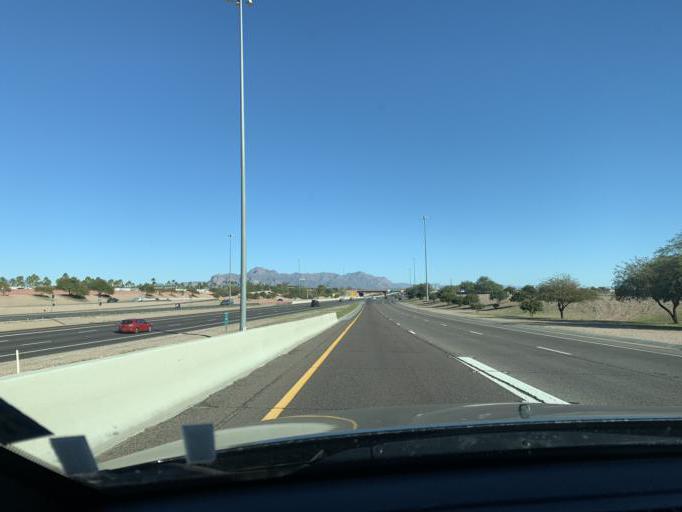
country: US
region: Arizona
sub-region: Pinal County
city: Apache Junction
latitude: 33.3862
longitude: -111.6401
